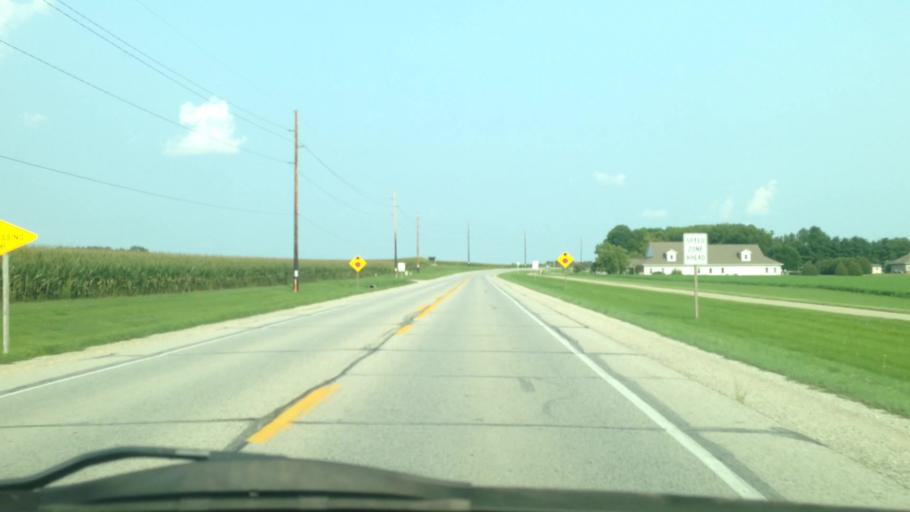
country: US
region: Iowa
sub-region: Benton County
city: Walford
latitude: 41.8034
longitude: -91.8820
